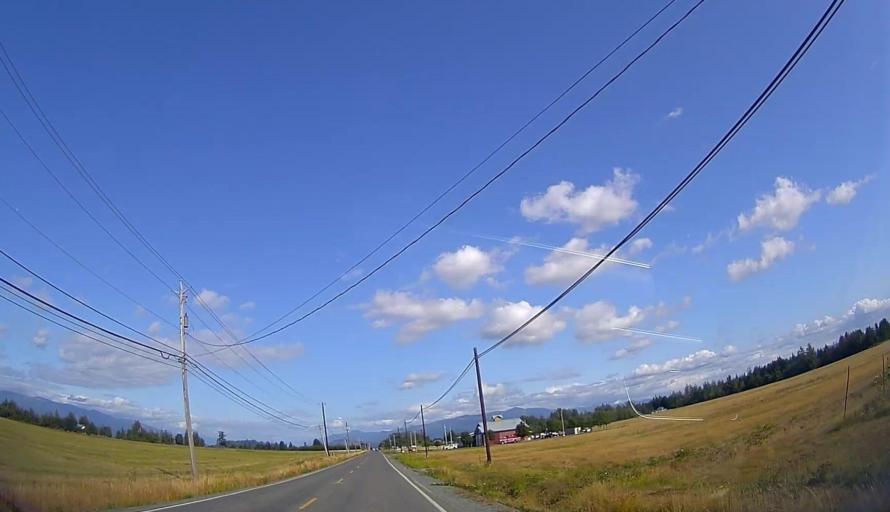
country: US
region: Washington
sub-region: Skagit County
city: Burlington
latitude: 48.4723
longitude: -122.3982
